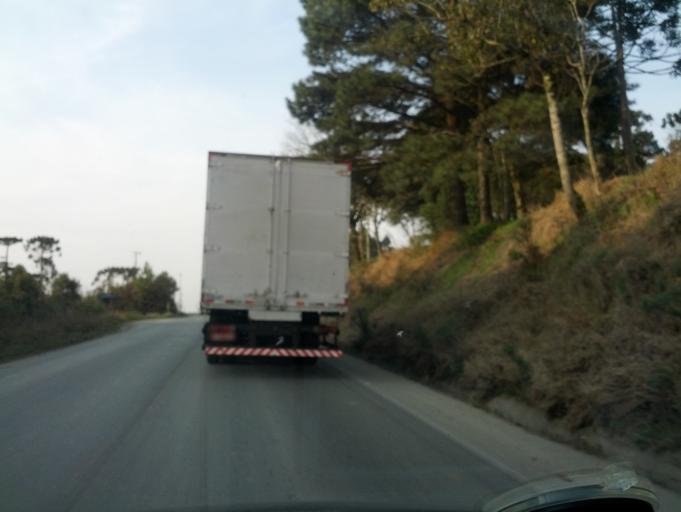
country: BR
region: Santa Catarina
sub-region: Otacilio Costa
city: Otacilio Costa
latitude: -27.5254
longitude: -50.1376
